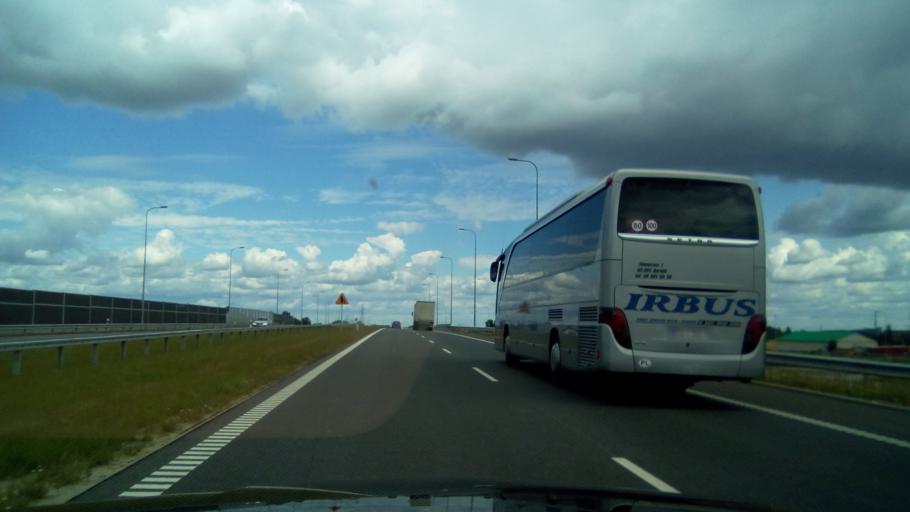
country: PL
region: Kujawsko-Pomorskie
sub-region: Powiat zninski
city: Znin
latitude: 52.8489
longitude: 17.6927
